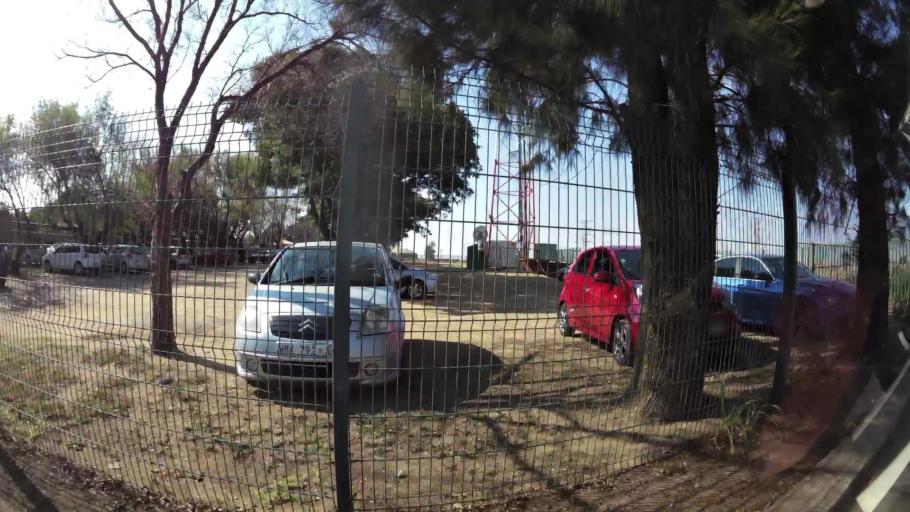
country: ZA
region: Gauteng
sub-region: Ekurhuleni Metropolitan Municipality
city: Benoni
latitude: -26.1442
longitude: 28.3975
